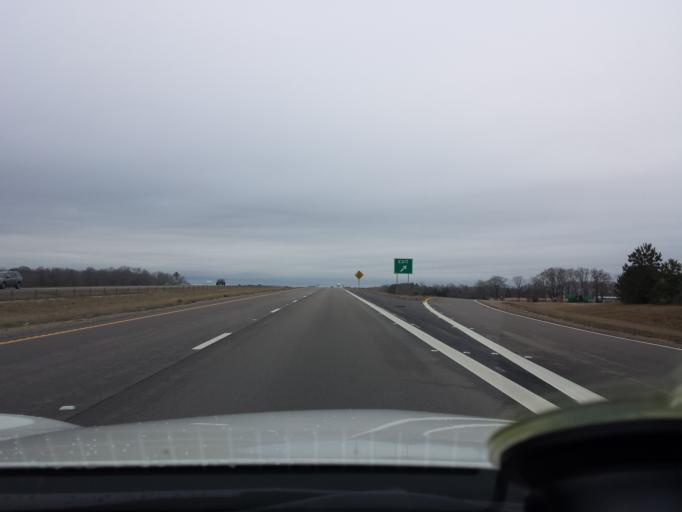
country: US
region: Mississippi
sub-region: Lee County
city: Shannon
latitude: 34.1505
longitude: -88.7023
